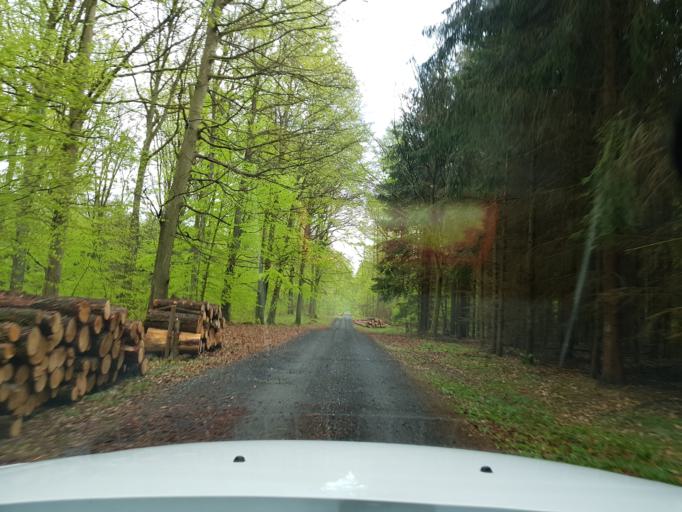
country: PL
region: West Pomeranian Voivodeship
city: Trzcinsko Zdroj
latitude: 52.9957
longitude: 14.6495
